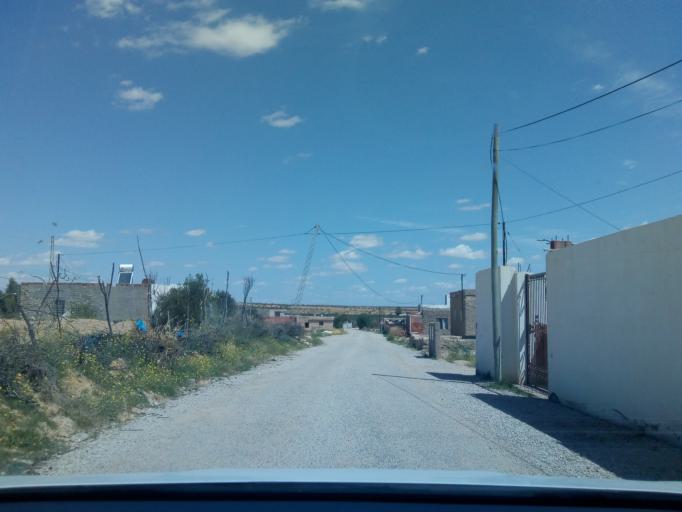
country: TN
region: Safaqis
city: Sfax
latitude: 34.7342
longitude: 10.4926
